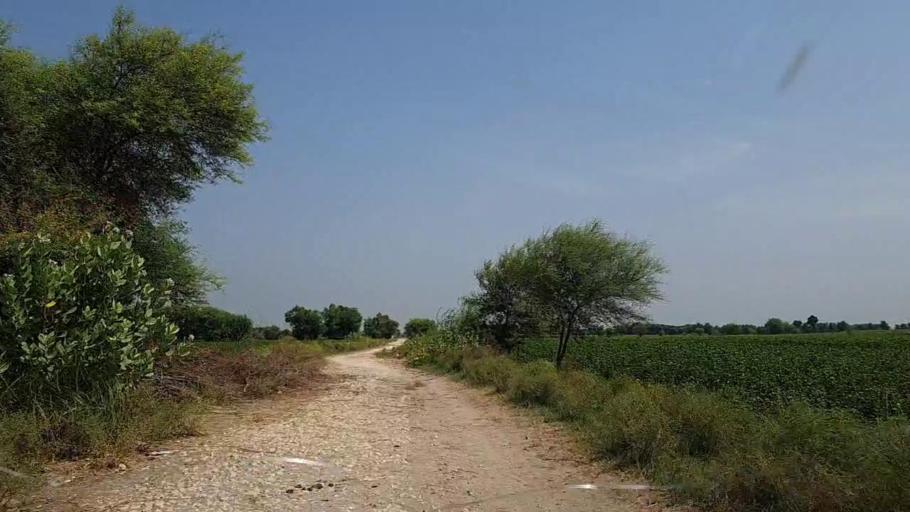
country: PK
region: Sindh
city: Adilpur
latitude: 27.8369
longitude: 69.2819
